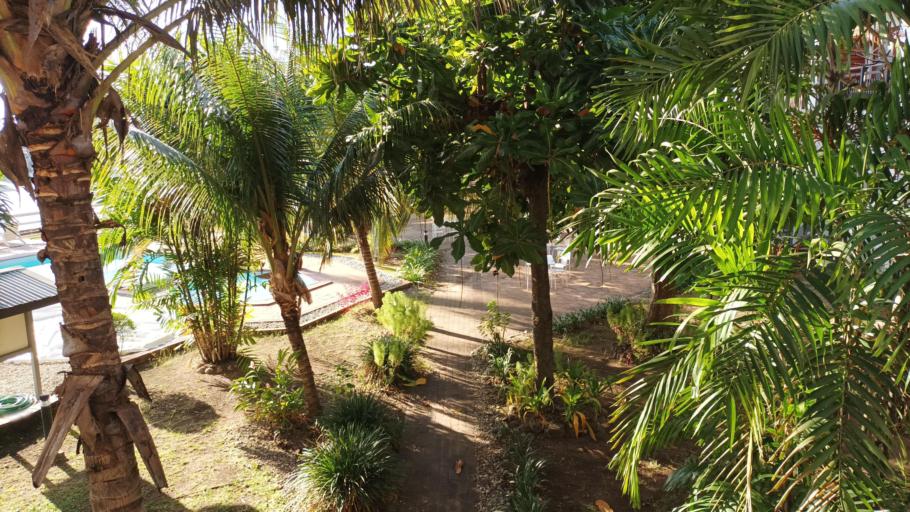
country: SB
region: Guadalcanal
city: Honiara
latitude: -9.4297
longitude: 159.9534
